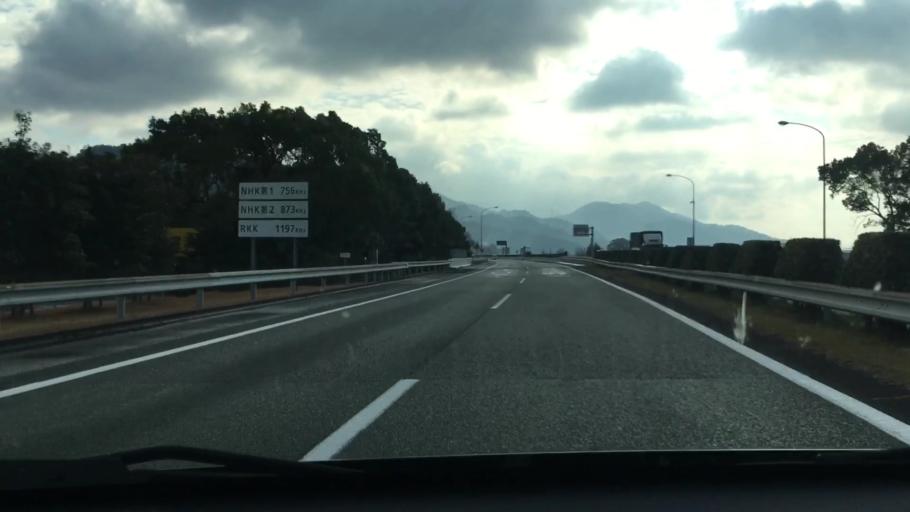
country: JP
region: Kumamoto
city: Yatsushiro
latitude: 32.5135
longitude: 130.6482
